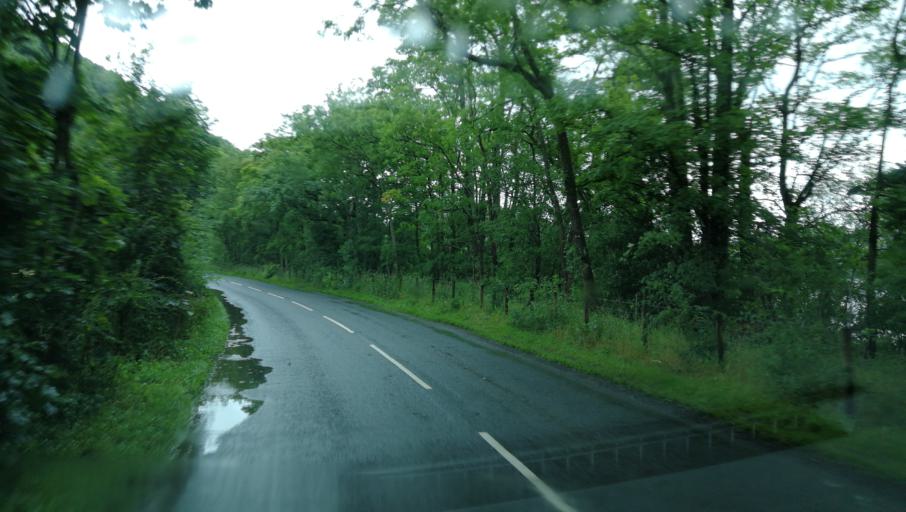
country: GB
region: England
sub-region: Cumbria
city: Penrith
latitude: 54.6055
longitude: -2.8406
